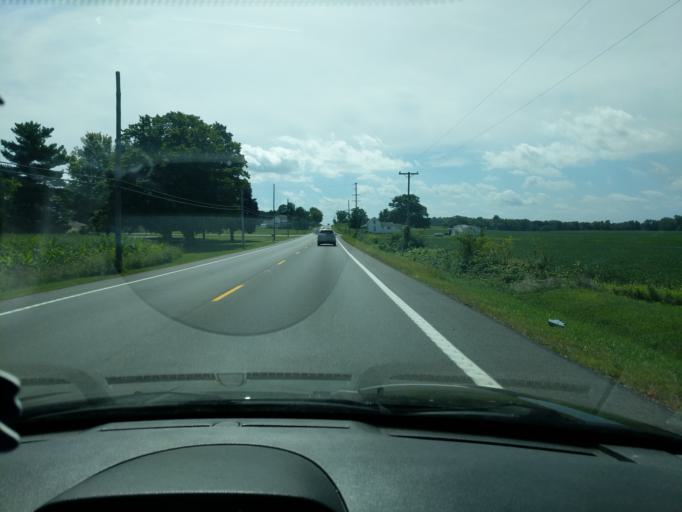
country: US
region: Ohio
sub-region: Logan County
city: Bellefontaine
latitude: 40.3154
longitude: -83.7603
